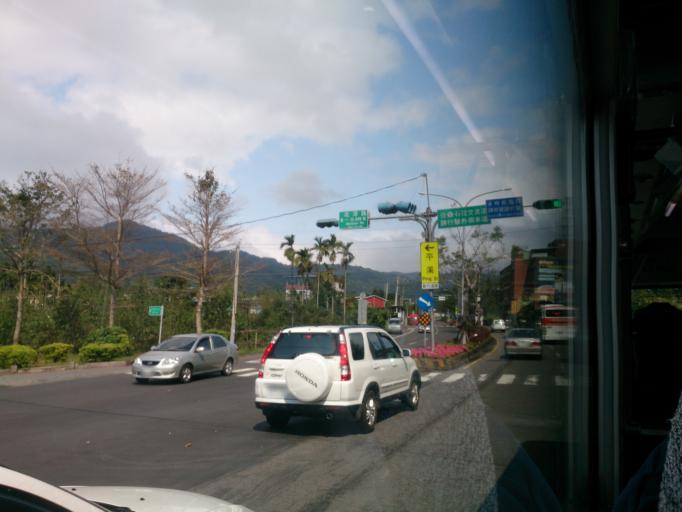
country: TW
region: Taipei
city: Taipei
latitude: 25.0019
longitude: 121.6267
